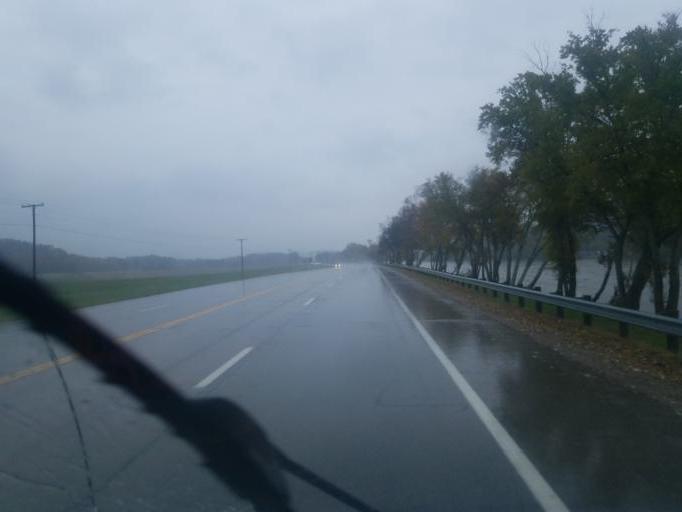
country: US
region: Ohio
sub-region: Muskingum County
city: South Zanesville
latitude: 39.8721
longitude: -81.9473
